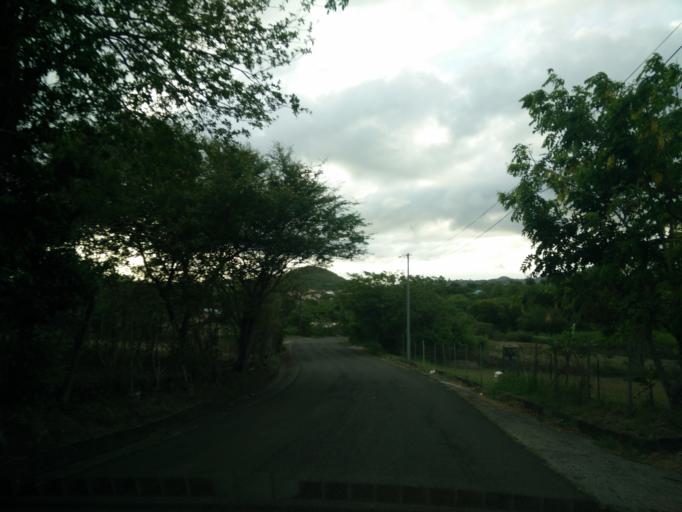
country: MQ
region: Martinique
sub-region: Martinique
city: Le Marin
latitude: 14.4533
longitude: -60.8410
